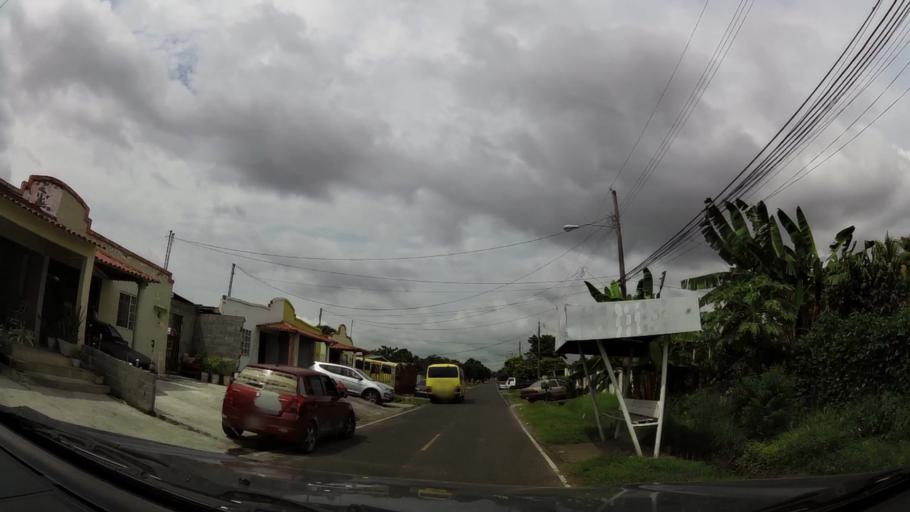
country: PA
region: Panama
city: San Miguelito
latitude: 9.0459
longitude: -79.4227
